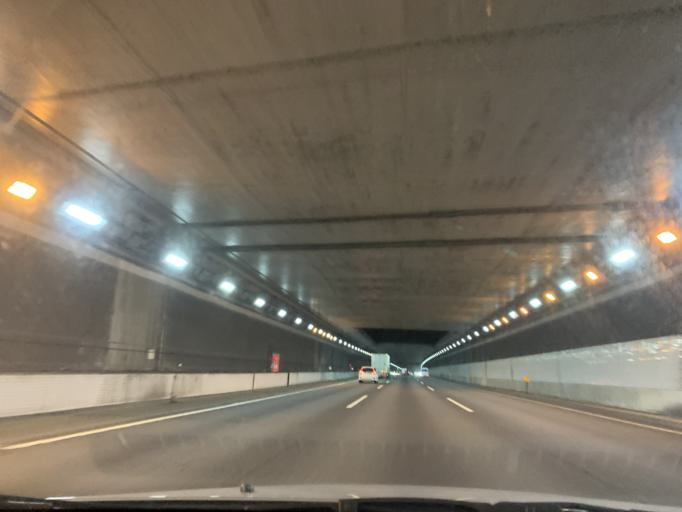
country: JP
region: Chiba
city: Nagareyama
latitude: 35.8929
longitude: 139.9173
